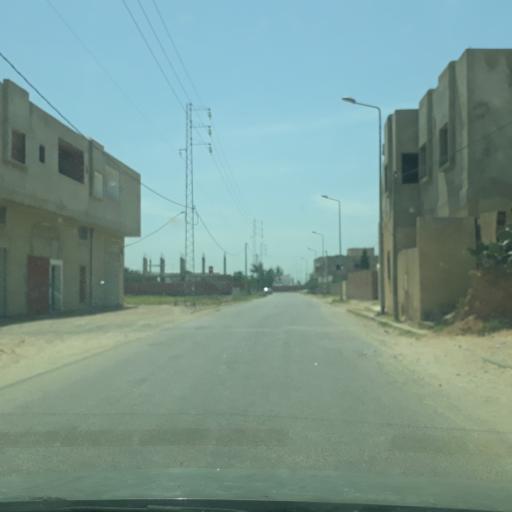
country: TN
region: Safaqis
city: Al Qarmadah
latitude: 34.8257
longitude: 10.7847
